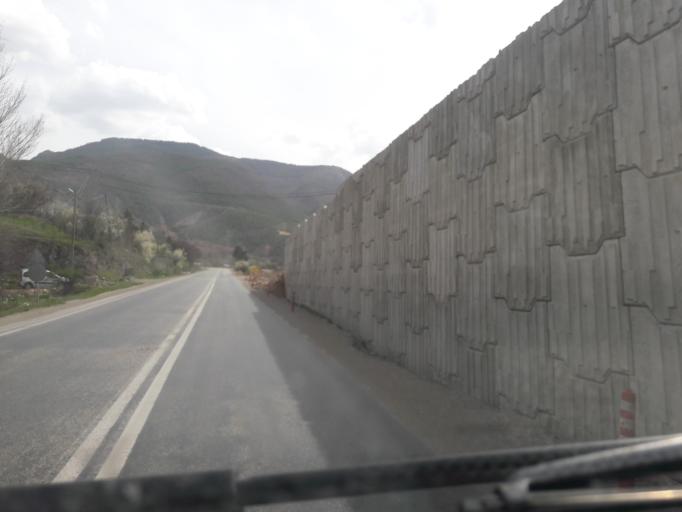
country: TR
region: Gumushane
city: Kale
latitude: 40.4039
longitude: 39.6072
